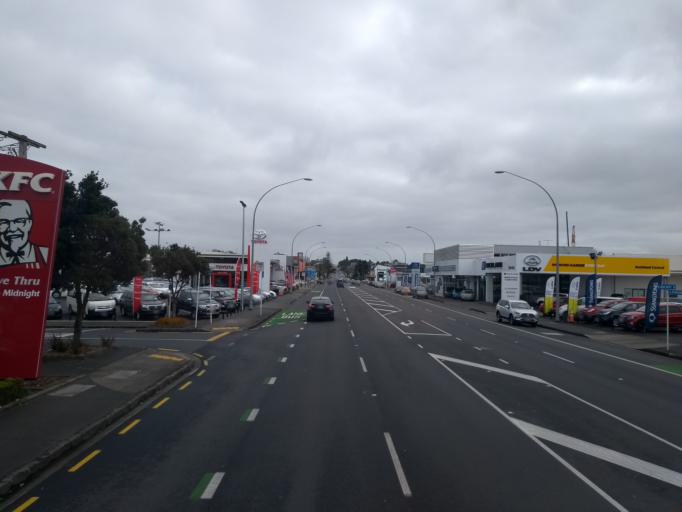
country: NZ
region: Auckland
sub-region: Auckland
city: Auckland
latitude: -36.8925
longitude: 174.7968
